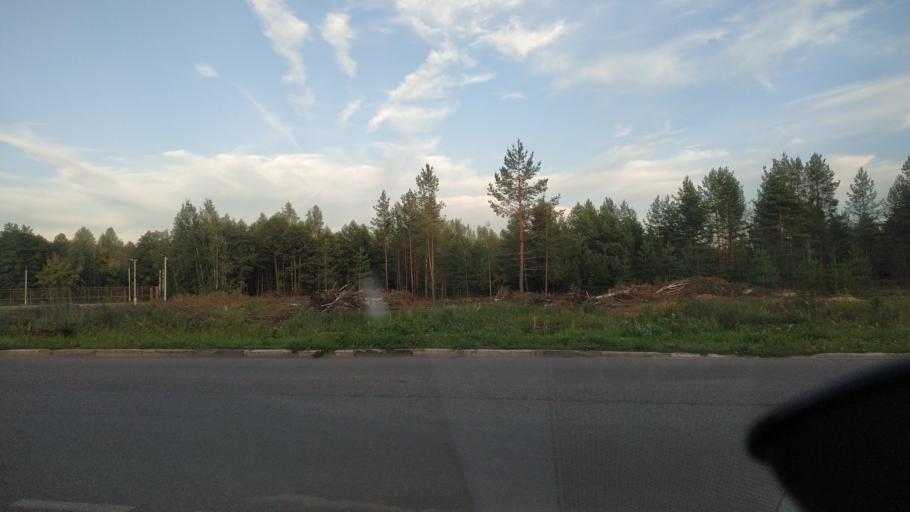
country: RU
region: Moskovskaya
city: Roshal'
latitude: 55.6620
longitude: 39.8575
